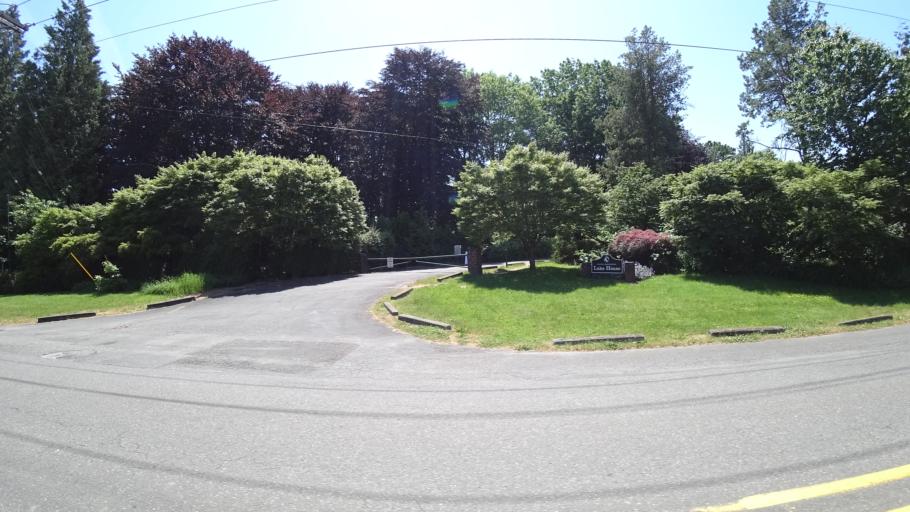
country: US
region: Oregon
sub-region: Multnomah County
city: Fairview
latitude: 45.5550
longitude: -122.4438
